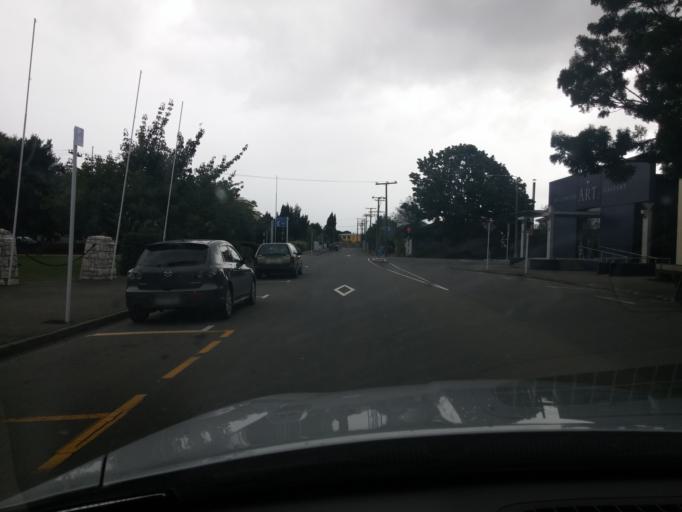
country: NZ
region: Marlborough
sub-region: Marlborough District
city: Blenheim
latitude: -41.5114
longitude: 173.9545
